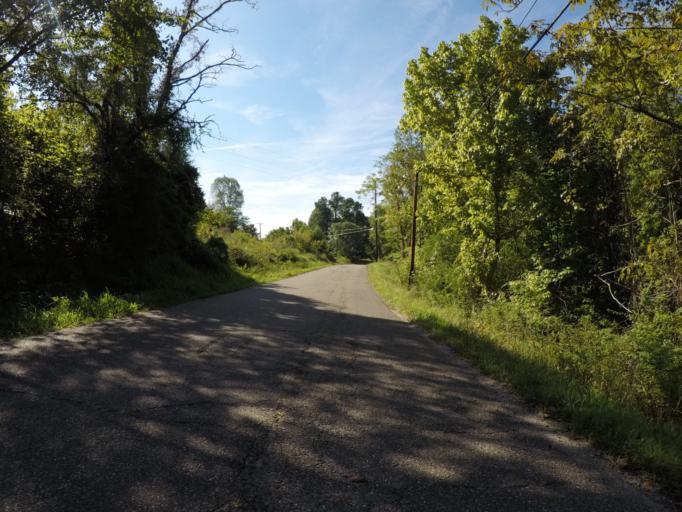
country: US
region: West Virginia
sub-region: Cabell County
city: Huntington
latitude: 38.4646
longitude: -82.4632
